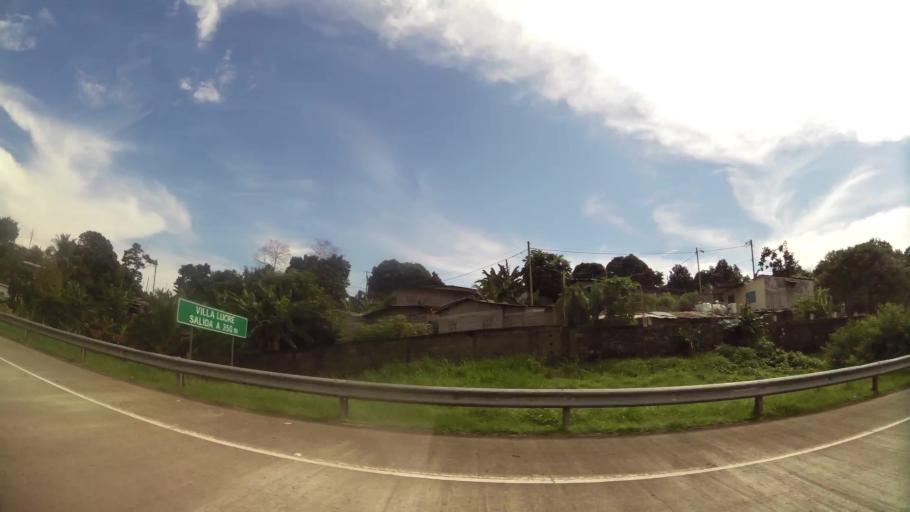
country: PA
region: Panama
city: San Miguelito
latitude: 9.0713
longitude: -79.4841
